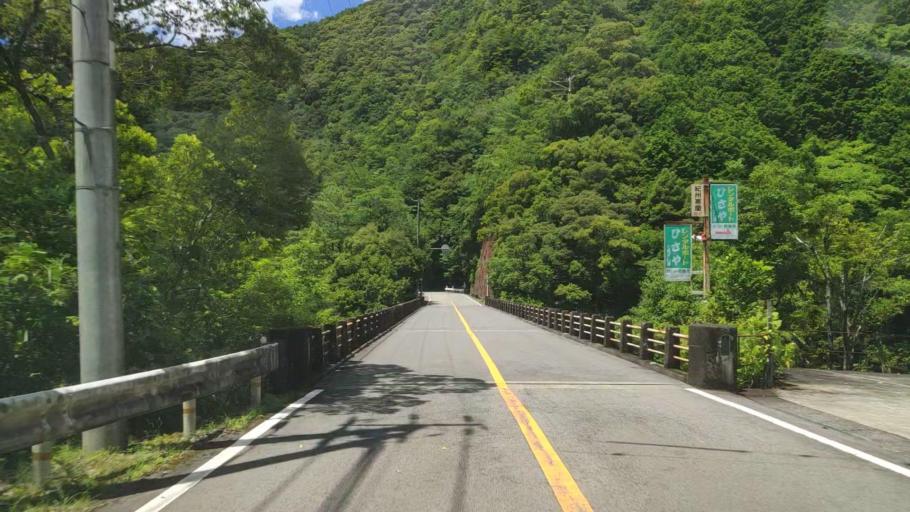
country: JP
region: Mie
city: Owase
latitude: 33.9984
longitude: 136.0174
